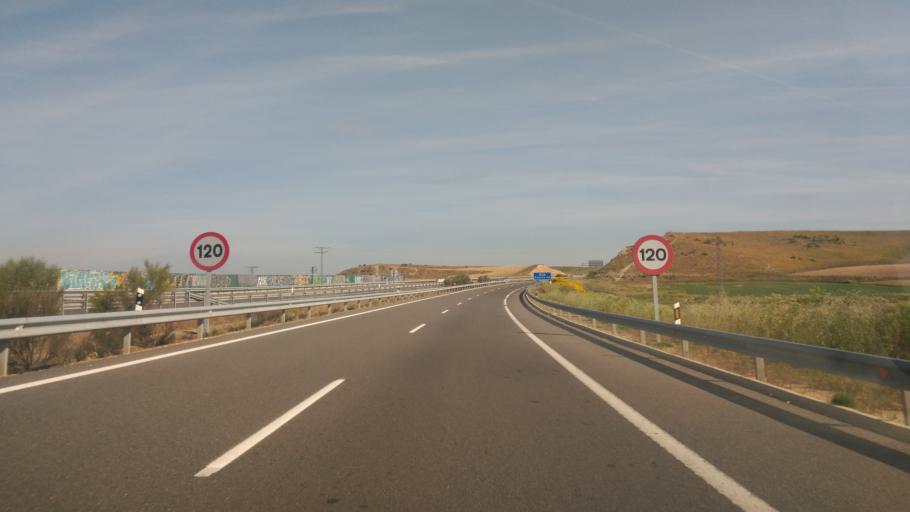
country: ES
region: Castille and Leon
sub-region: Provincia de Salamanca
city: Villamayor
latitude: 41.0021
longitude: -5.6772
